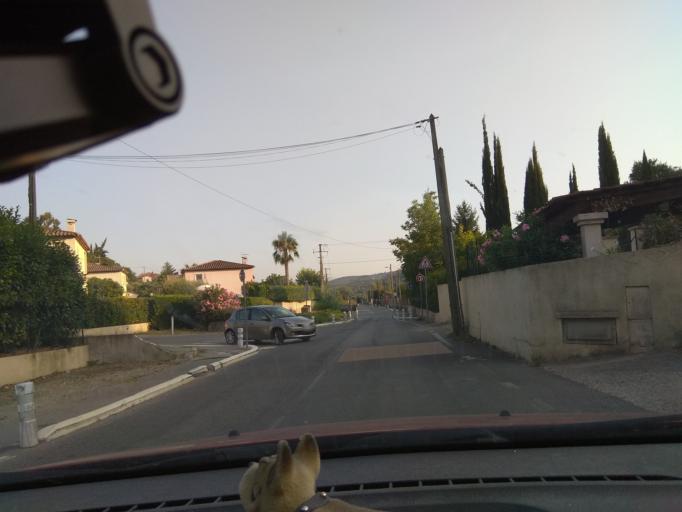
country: FR
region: Provence-Alpes-Cote d'Azur
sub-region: Departement des Alpes-Maritimes
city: La Colle-sur-Loup
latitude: 43.6812
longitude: 7.1066
